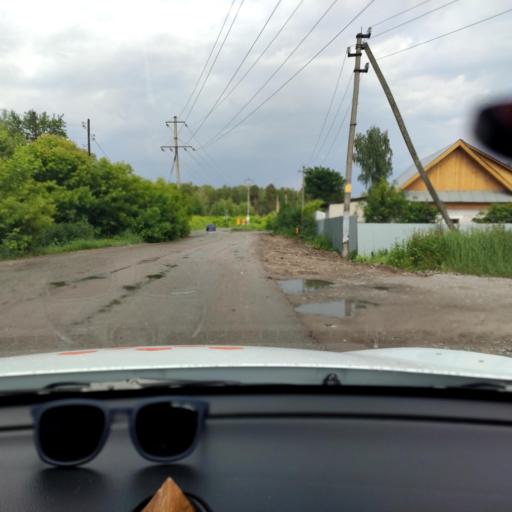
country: RU
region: Tatarstan
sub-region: Zelenodol'skiy Rayon
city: Vasil'yevo
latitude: 55.8360
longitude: 48.6849
